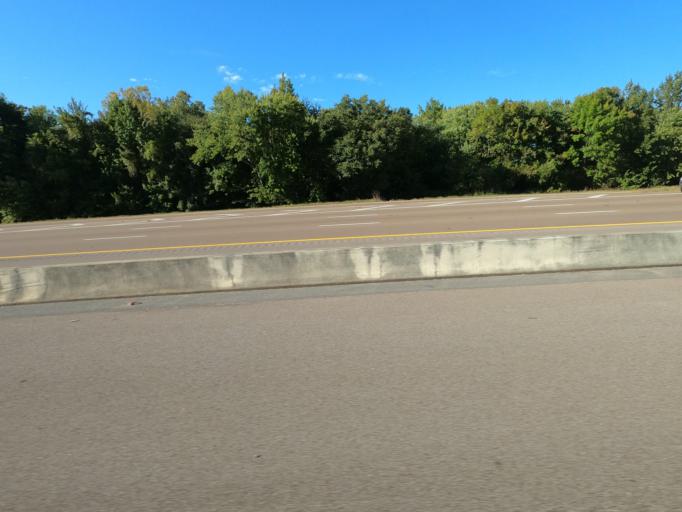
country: US
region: Tennessee
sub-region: Shelby County
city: Bartlett
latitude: 35.1911
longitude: -89.9307
